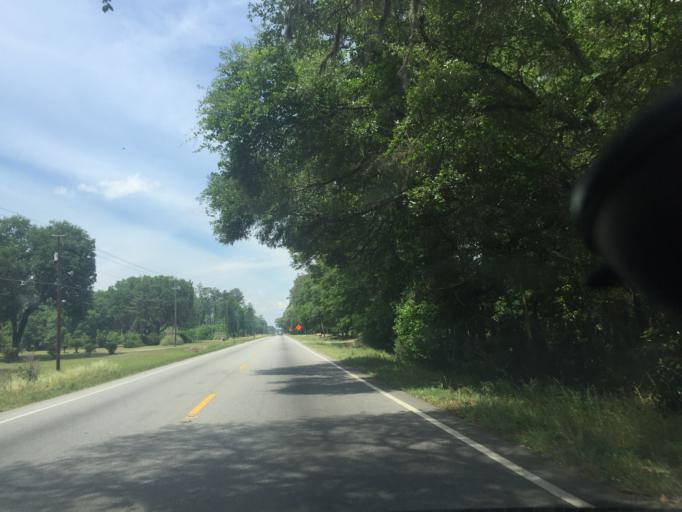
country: US
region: Georgia
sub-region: Chatham County
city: Bloomingdale
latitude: 32.1551
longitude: -81.3580
